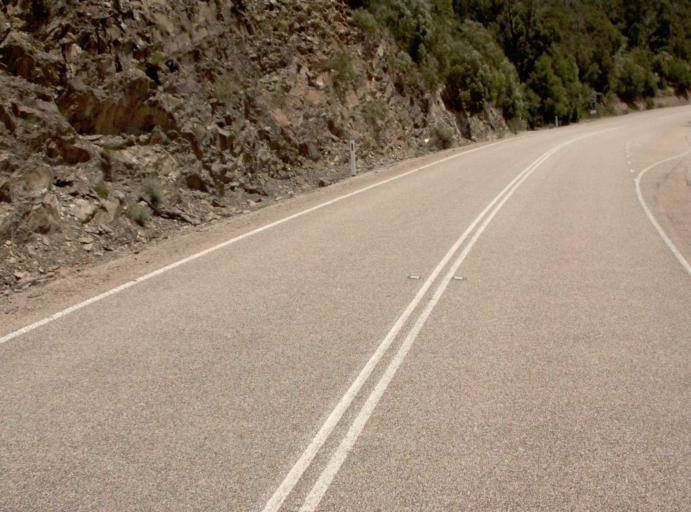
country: AU
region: Victoria
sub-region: East Gippsland
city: Lakes Entrance
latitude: -37.5525
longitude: 147.8696
